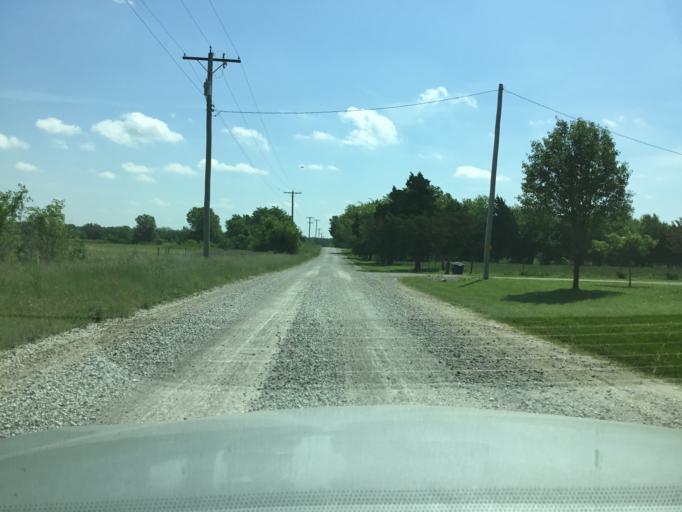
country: US
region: Kansas
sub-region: Labette County
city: Parsons
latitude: 37.3110
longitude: -95.2586
